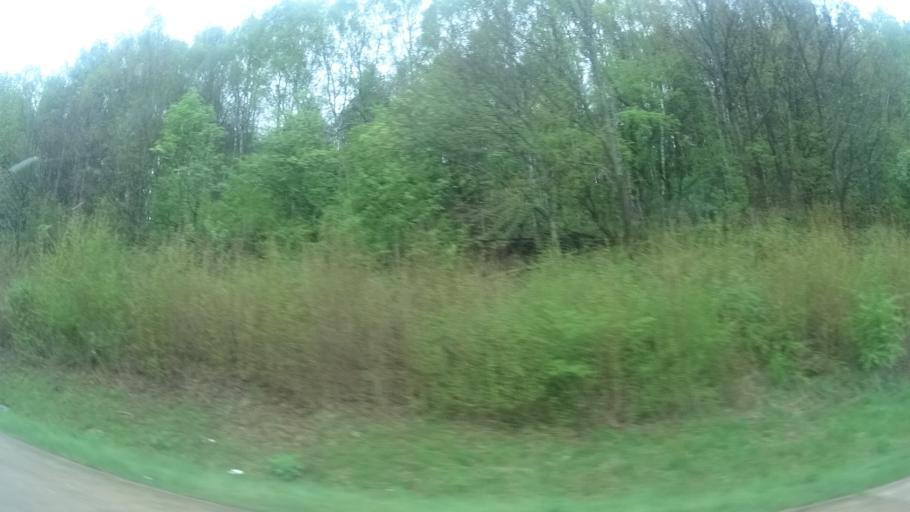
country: DE
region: Hesse
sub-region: Regierungsbezirk Kassel
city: Kirchheim
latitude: 50.8049
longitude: 9.5276
